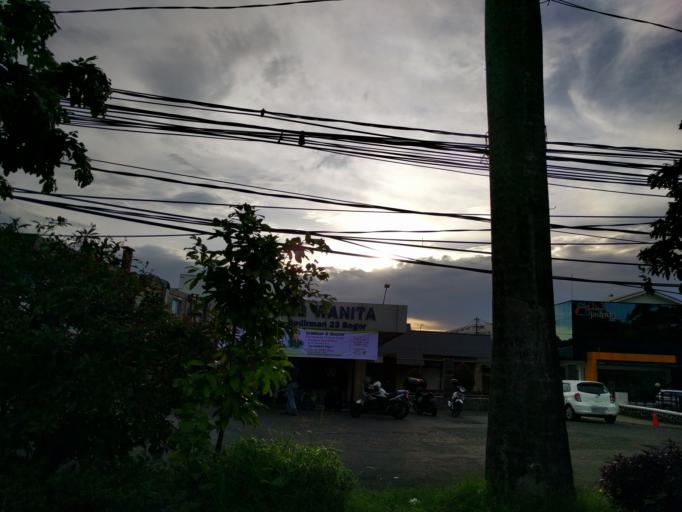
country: ID
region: West Java
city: Bogor
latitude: -6.5881
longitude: 106.7969
